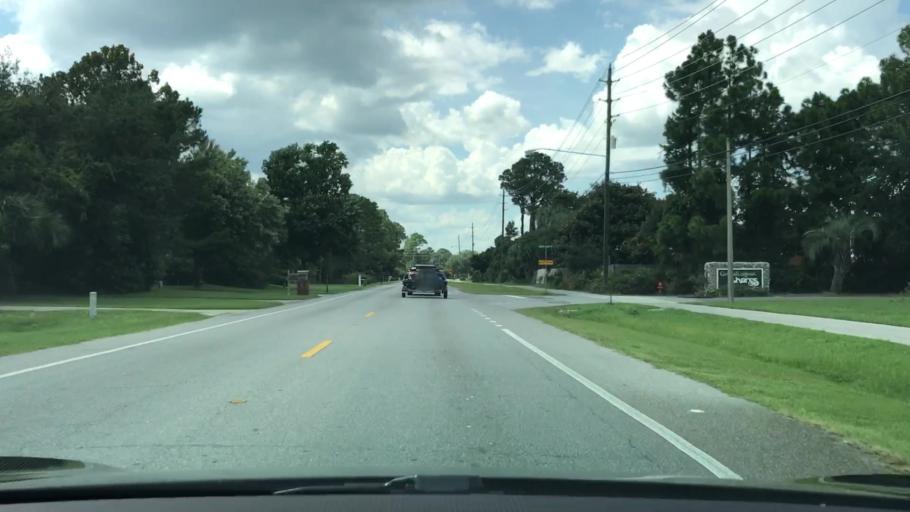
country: US
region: Florida
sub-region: Bay County
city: Panama City Beach
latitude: 30.1690
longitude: -85.7834
